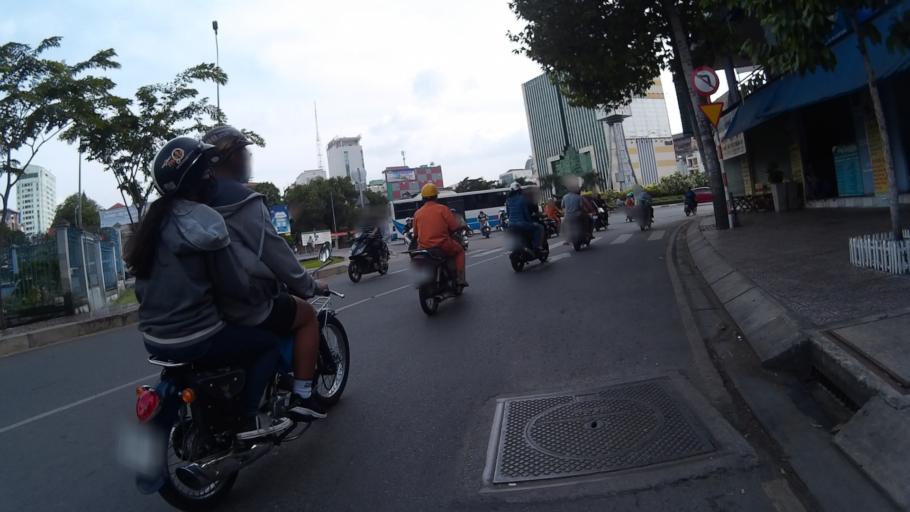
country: VN
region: Ho Chi Minh City
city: Quan Binh Thanh
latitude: 10.7930
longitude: 106.6994
